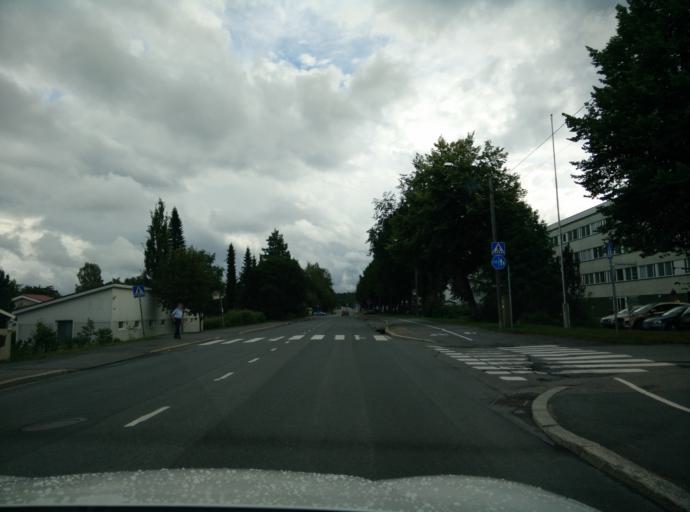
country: FI
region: Haeme
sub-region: Haemeenlinna
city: Haemeenlinna
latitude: 60.9988
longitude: 24.4277
